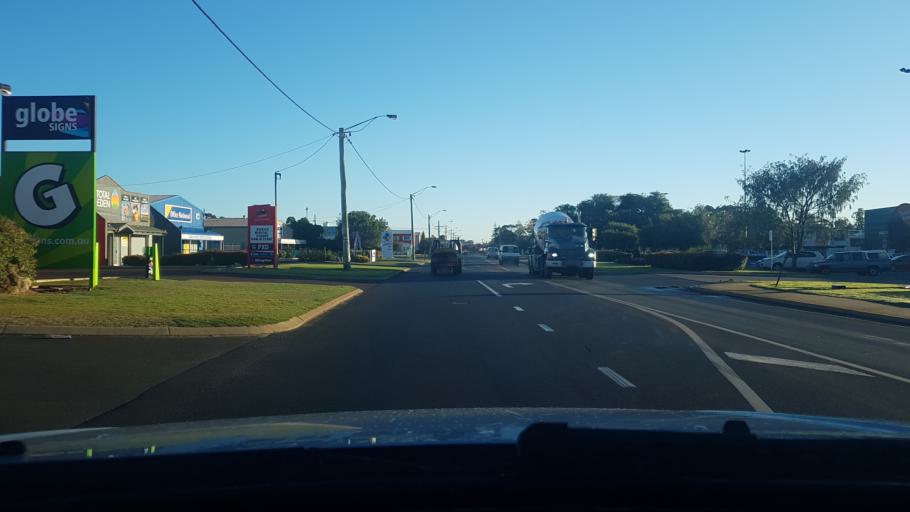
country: AU
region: Western Australia
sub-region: Busselton
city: Busselton
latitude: -33.6678
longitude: 115.3495
